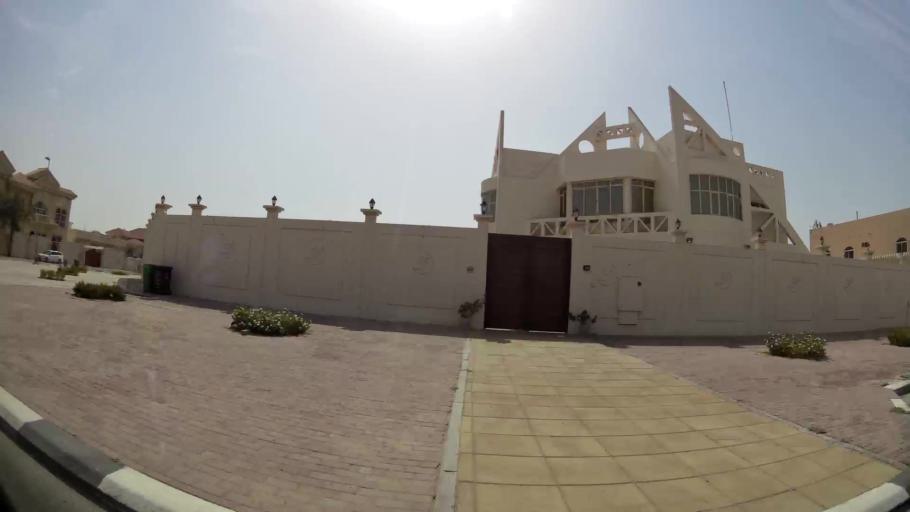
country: AE
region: Ash Shariqah
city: Sharjah
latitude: 25.2505
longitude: 55.4342
